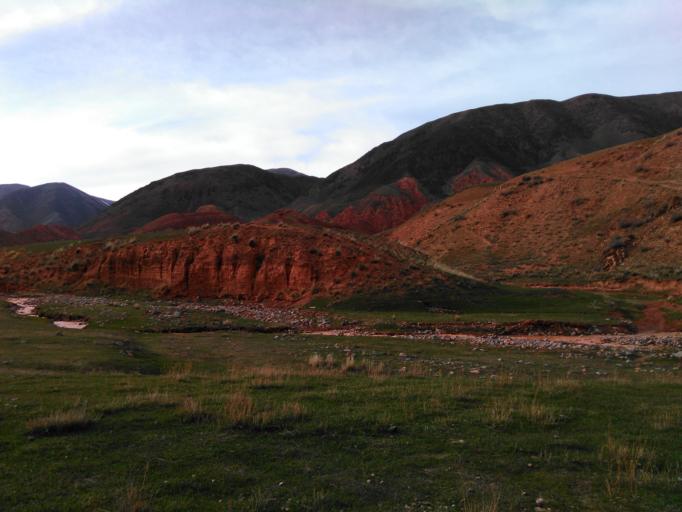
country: KG
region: Chuy
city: Bystrovka
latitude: 42.5642
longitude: 75.6259
